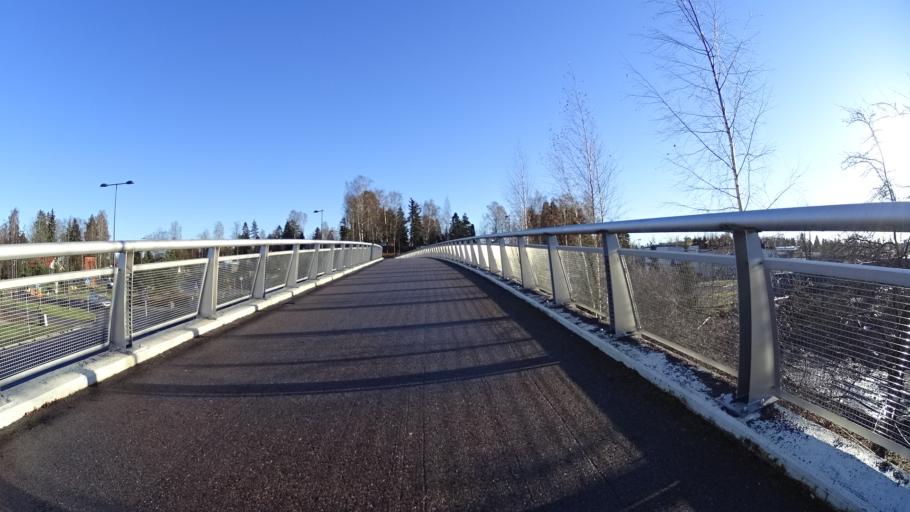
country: FI
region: Uusimaa
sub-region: Helsinki
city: Teekkarikylae
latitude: 60.2297
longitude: 24.8237
